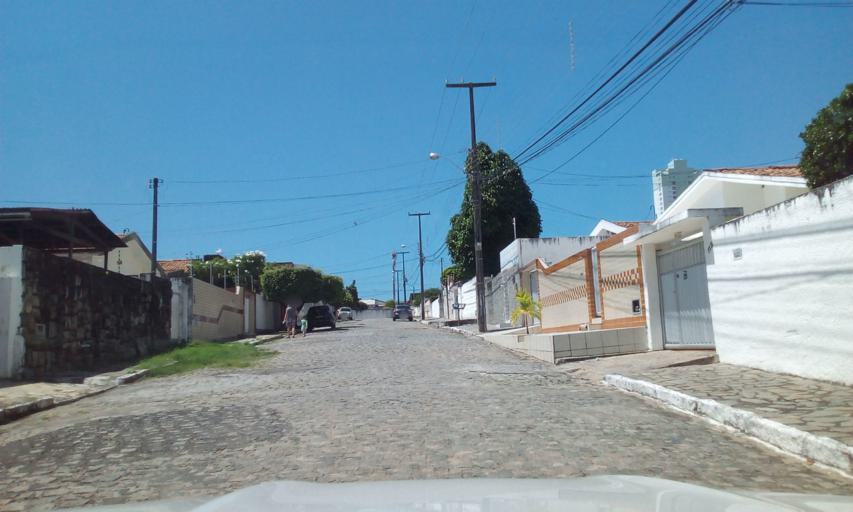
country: BR
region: Paraiba
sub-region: Joao Pessoa
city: Joao Pessoa
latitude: -7.1120
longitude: -34.8409
